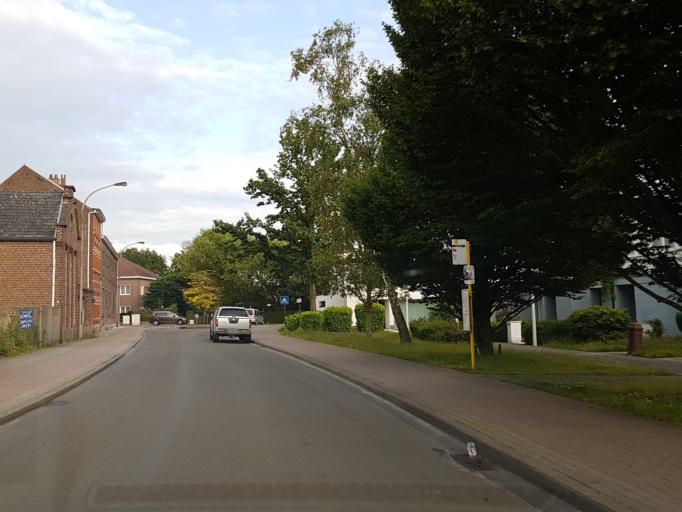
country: BE
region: Flanders
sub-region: Provincie Oost-Vlaanderen
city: Aalst
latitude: 50.9352
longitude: 4.0639
